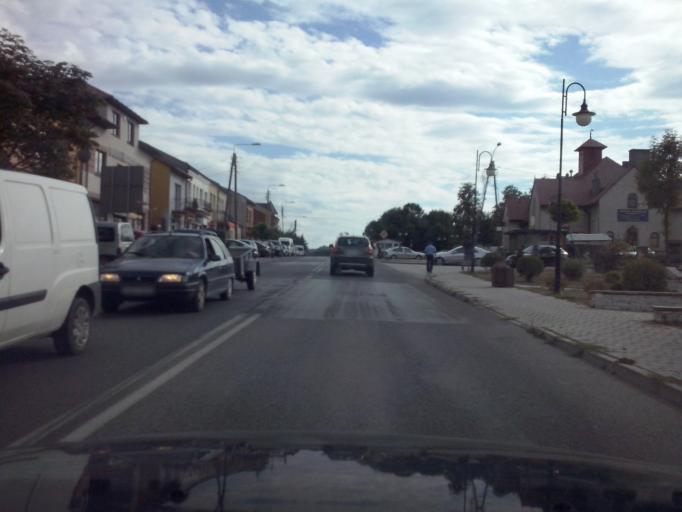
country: PL
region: Swietokrzyskie
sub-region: Powiat kielecki
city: Lagow
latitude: 50.7750
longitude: 21.0841
